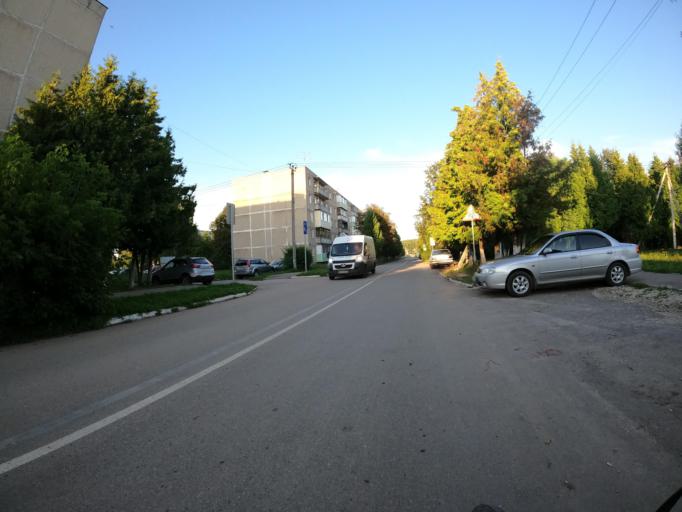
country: RU
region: Moskovskaya
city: Meshcherino
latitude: 55.1124
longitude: 38.3351
